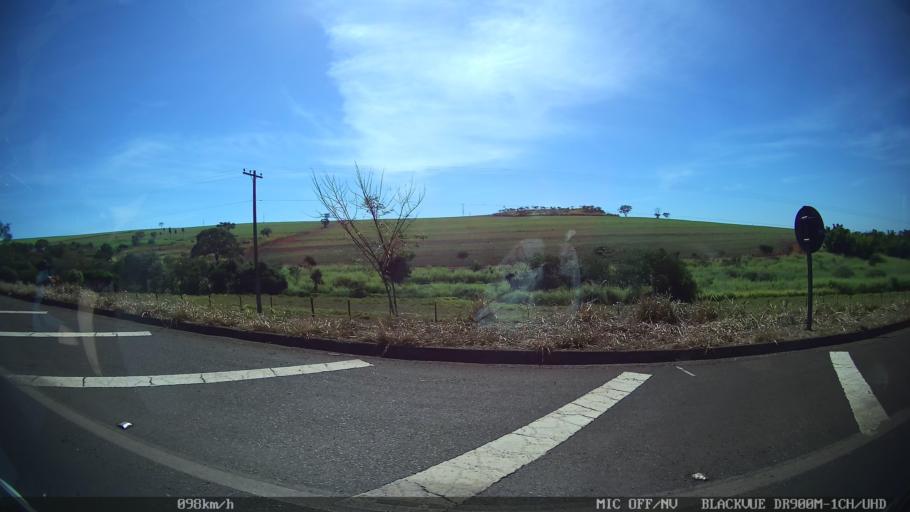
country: BR
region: Sao Paulo
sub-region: Ipua
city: Ipua
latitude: -20.4927
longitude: -48.0120
